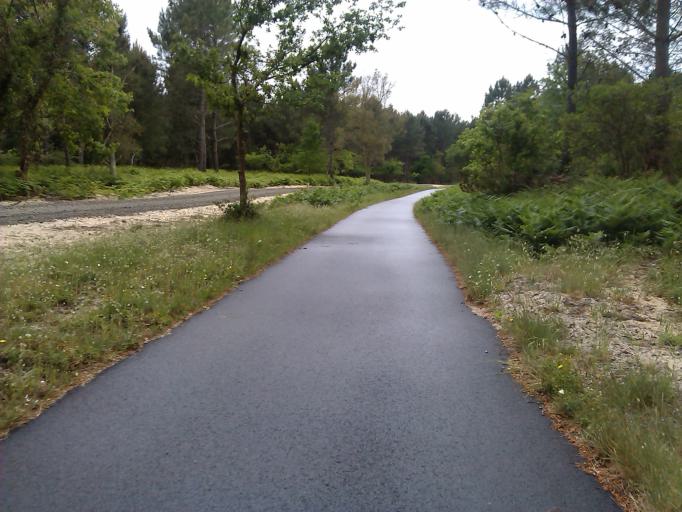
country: FR
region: Aquitaine
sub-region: Departement des Landes
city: Vielle-Saint-Girons
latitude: 43.9270
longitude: -1.3520
